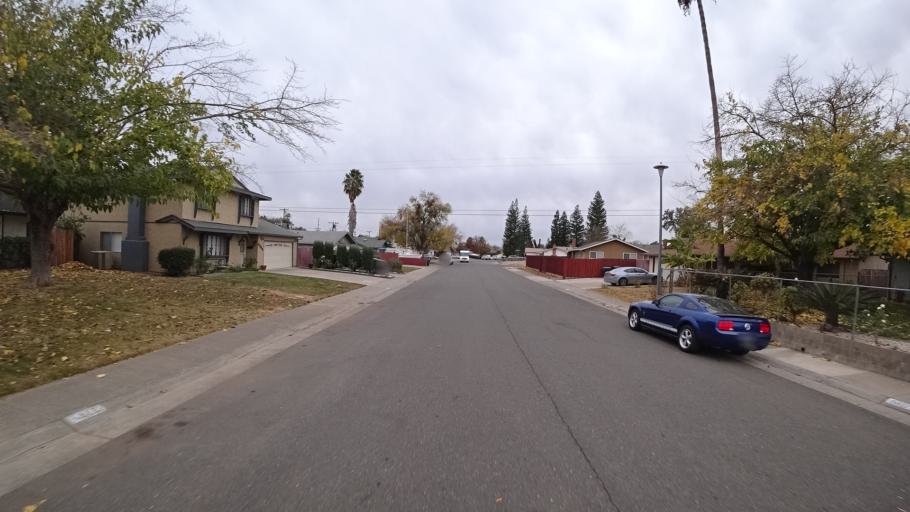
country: US
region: California
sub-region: Sacramento County
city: Antelope
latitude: 38.6895
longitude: -121.3068
